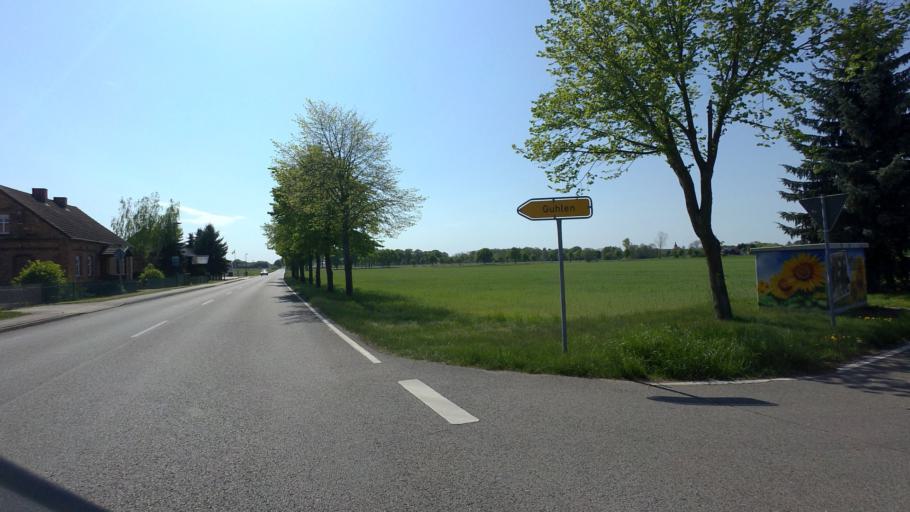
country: DE
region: Brandenburg
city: Neu Zauche
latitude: 52.0283
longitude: 14.0899
